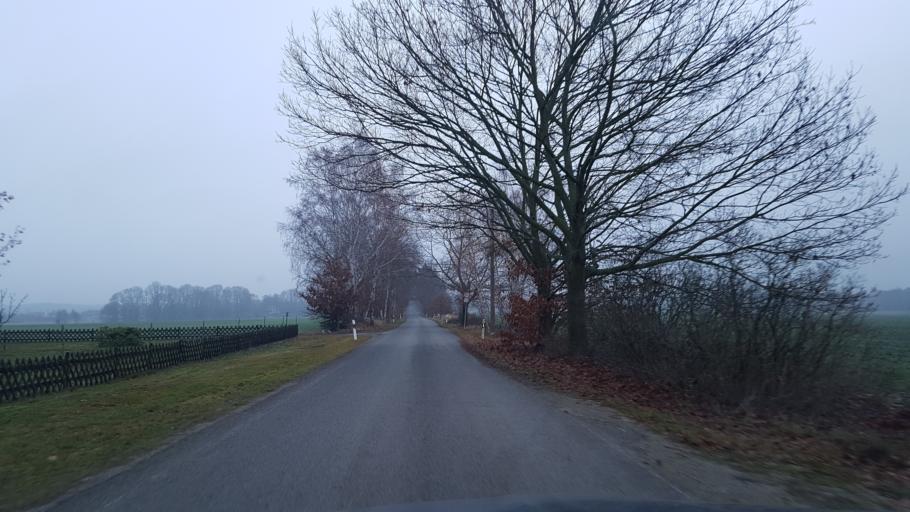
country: DE
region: Brandenburg
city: Ruckersdorf
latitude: 51.5477
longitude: 13.5839
